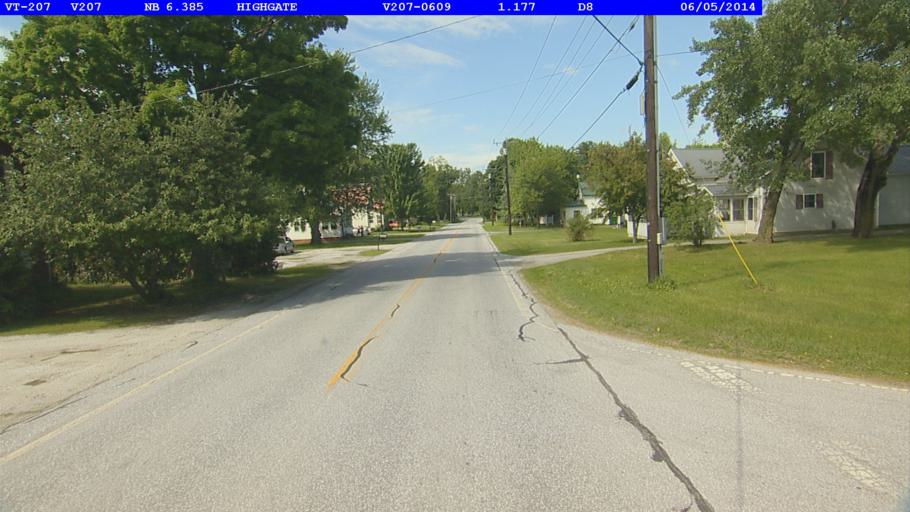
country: US
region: Vermont
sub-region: Franklin County
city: Swanton
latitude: 44.9276
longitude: -73.0503
